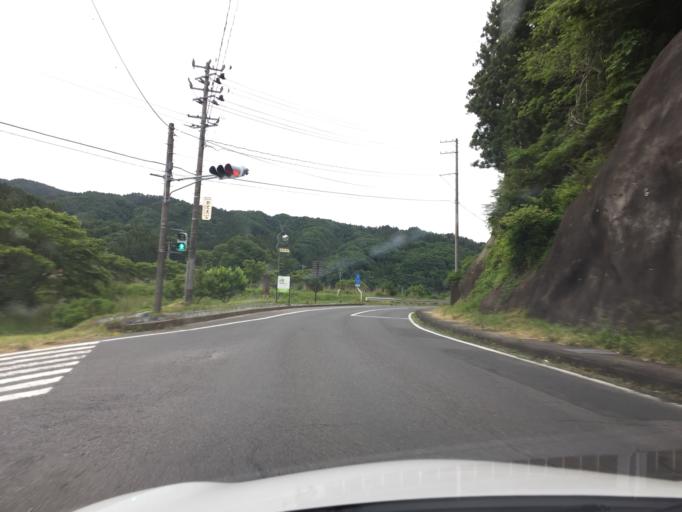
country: JP
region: Fukushima
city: Funehikimachi-funehiki
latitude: 37.3198
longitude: 140.6594
